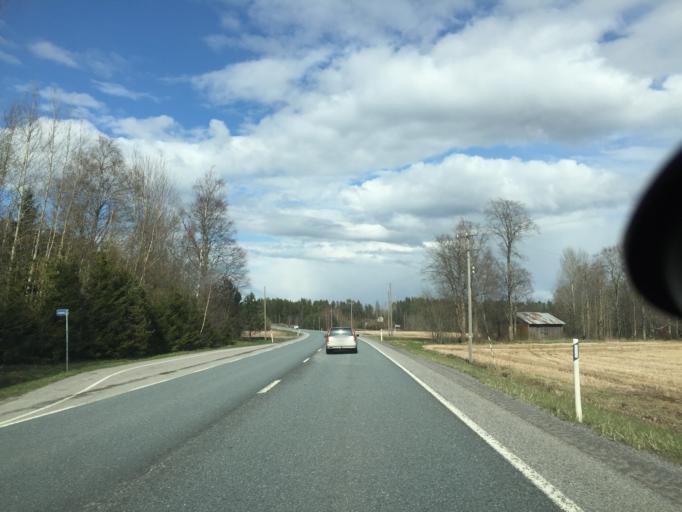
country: FI
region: Uusimaa
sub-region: Raaseporin
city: Inga
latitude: 60.1382
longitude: 23.8824
